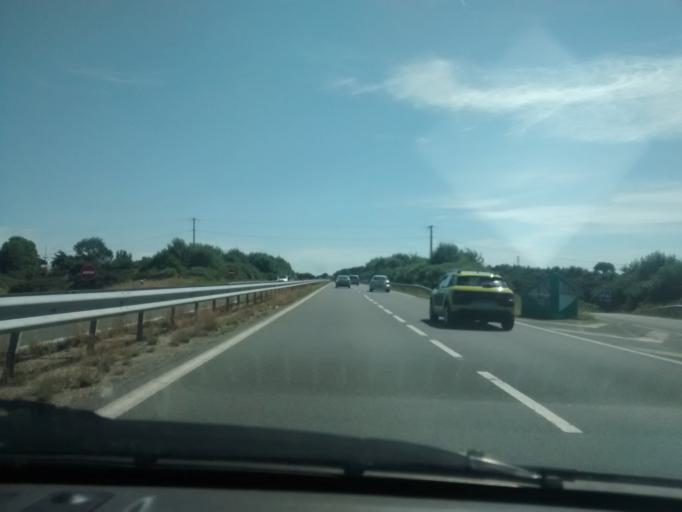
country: FR
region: Brittany
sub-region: Departement des Cotes-d'Armor
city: Rospez
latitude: 48.7060
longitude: -3.3796
